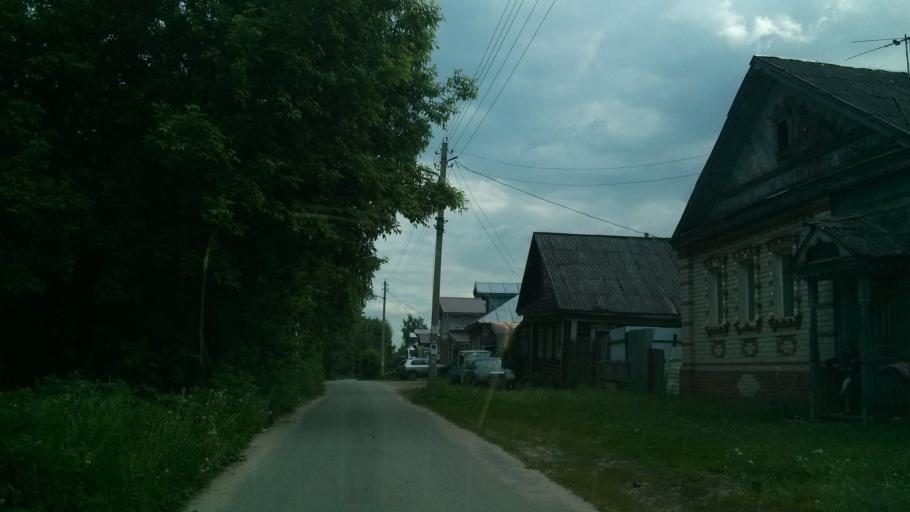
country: RU
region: Nizjnij Novgorod
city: Afonino
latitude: 56.2745
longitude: 44.1043
